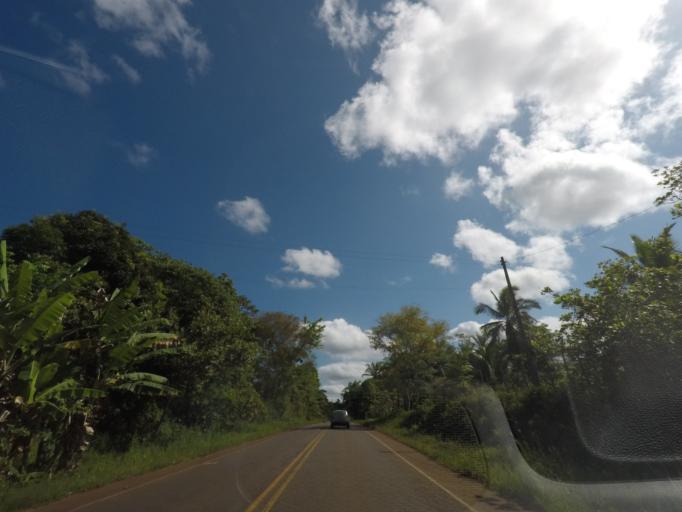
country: BR
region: Bahia
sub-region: Camamu
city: Camamu
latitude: -13.9054
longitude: -39.1330
